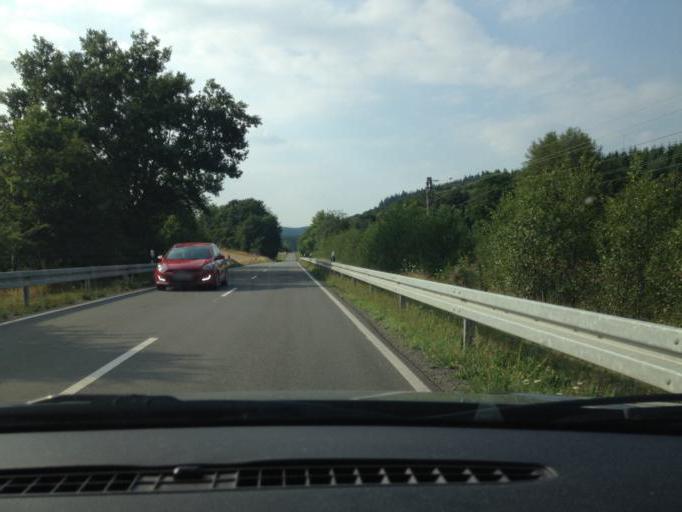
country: DE
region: Saarland
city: Nohfelden
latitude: 49.5662
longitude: 7.1224
